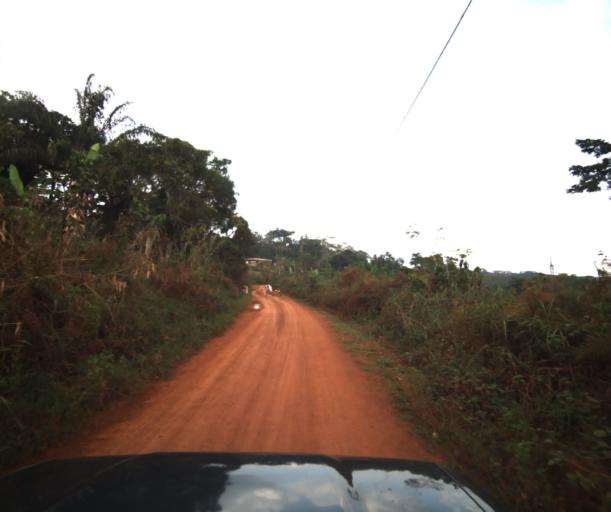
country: CM
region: Centre
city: Akono
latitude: 3.6027
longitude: 11.1860
